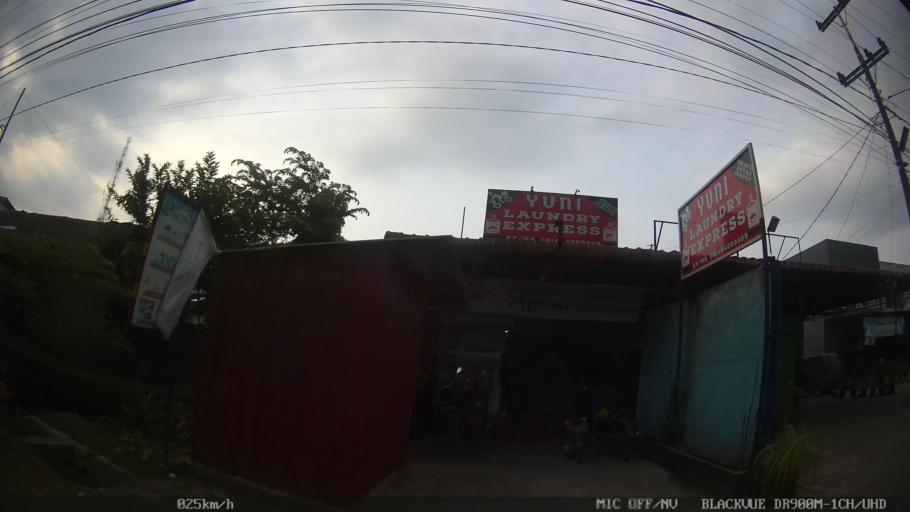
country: ID
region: North Sumatra
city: Sunggal
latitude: 3.5595
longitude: 98.5581
